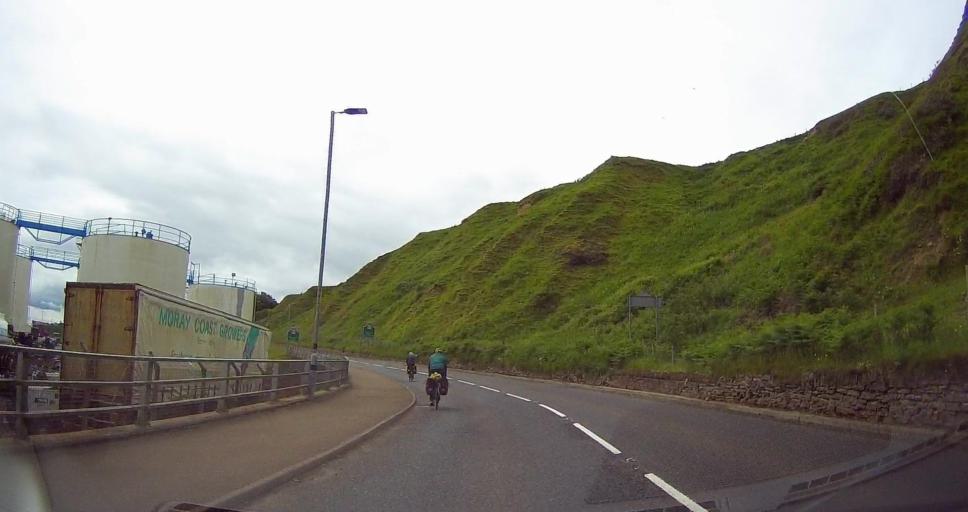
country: GB
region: Scotland
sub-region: Highland
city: Thurso
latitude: 58.6111
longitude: -3.5525
